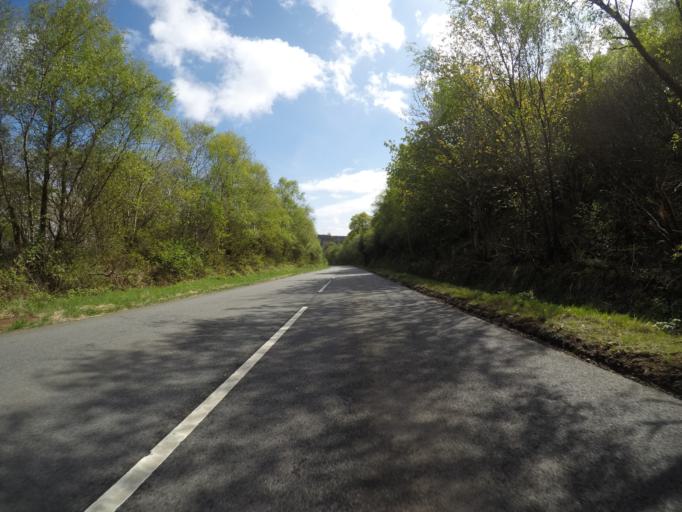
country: GB
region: Scotland
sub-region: Highland
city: Isle of Skye
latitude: 57.4599
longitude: -6.3292
